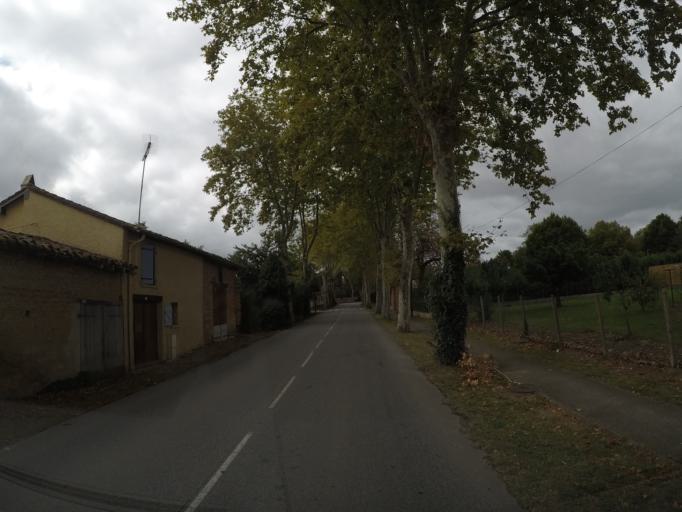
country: FR
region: Midi-Pyrenees
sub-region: Departement de la Haute-Garonne
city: Saint-Sulpice-sur-Leze
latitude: 43.3303
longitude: 1.3204
